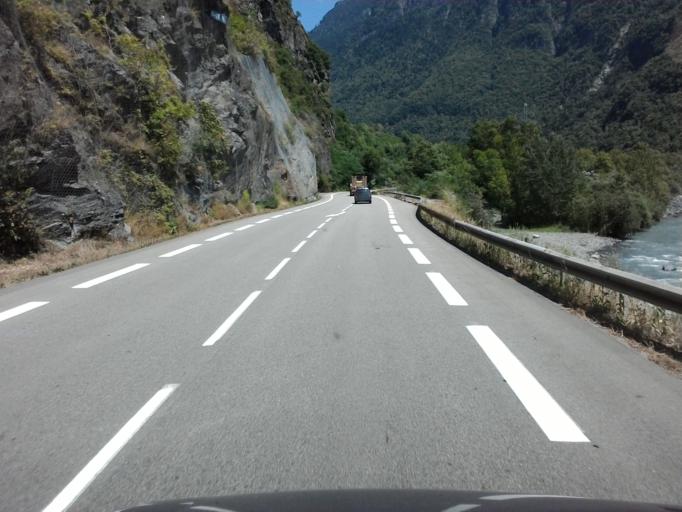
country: FR
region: Rhone-Alpes
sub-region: Departement de l'Isere
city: Vaulnaveys-le-Bas
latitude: 45.0525
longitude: 5.8424
